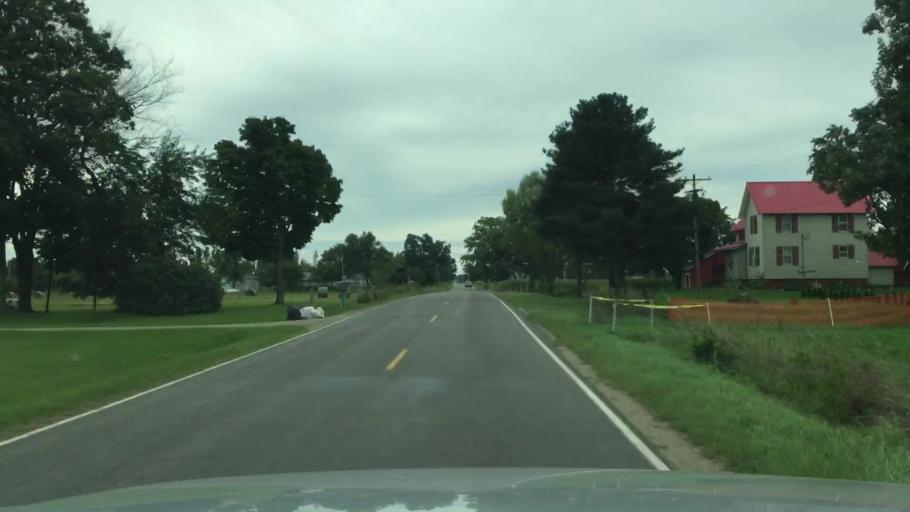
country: US
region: Michigan
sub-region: Shiawassee County
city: Durand
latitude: 43.0160
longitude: -83.9871
